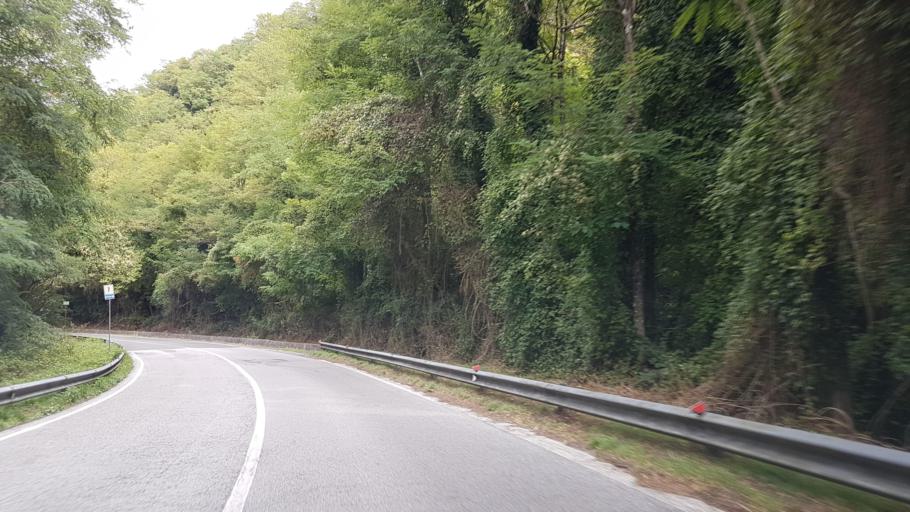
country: IT
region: Liguria
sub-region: Provincia di La Spezia
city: Carrodano
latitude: 44.2174
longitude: 9.6294
